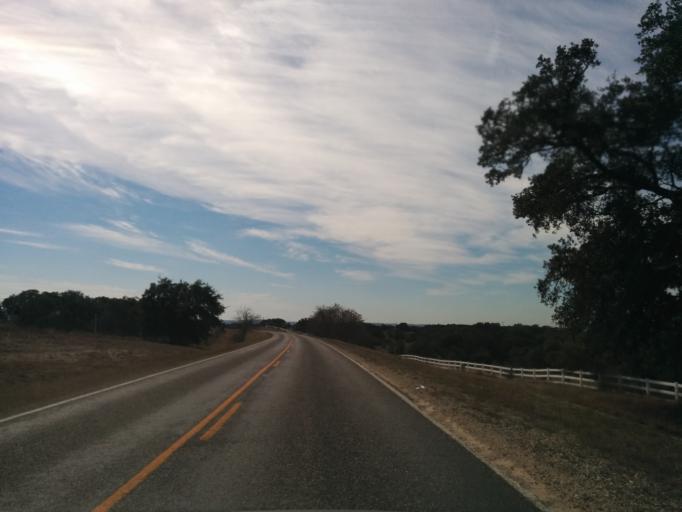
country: US
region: Texas
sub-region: Bexar County
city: Fair Oaks Ranch
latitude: 29.9277
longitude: -98.5708
